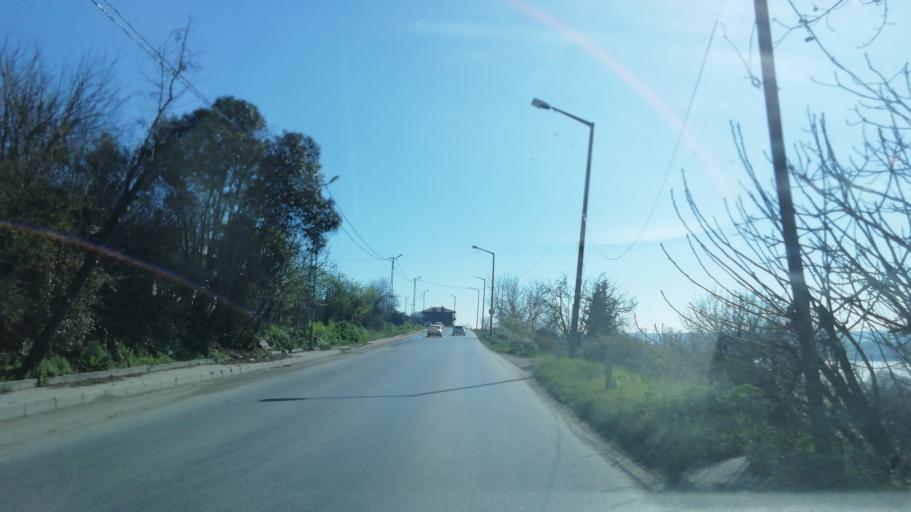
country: TR
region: Istanbul
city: Basaksehir
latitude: 41.0506
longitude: 28.7491
